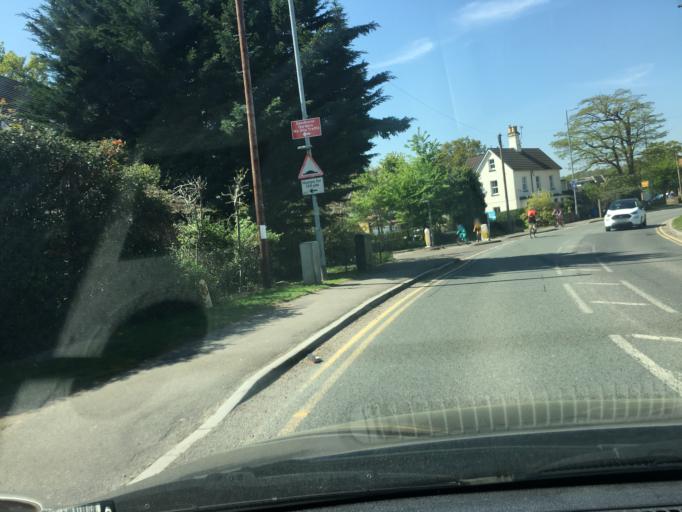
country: GB
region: England
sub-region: Bracknell Forest
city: Sandhurst
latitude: 51.3468
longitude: -0.8054
